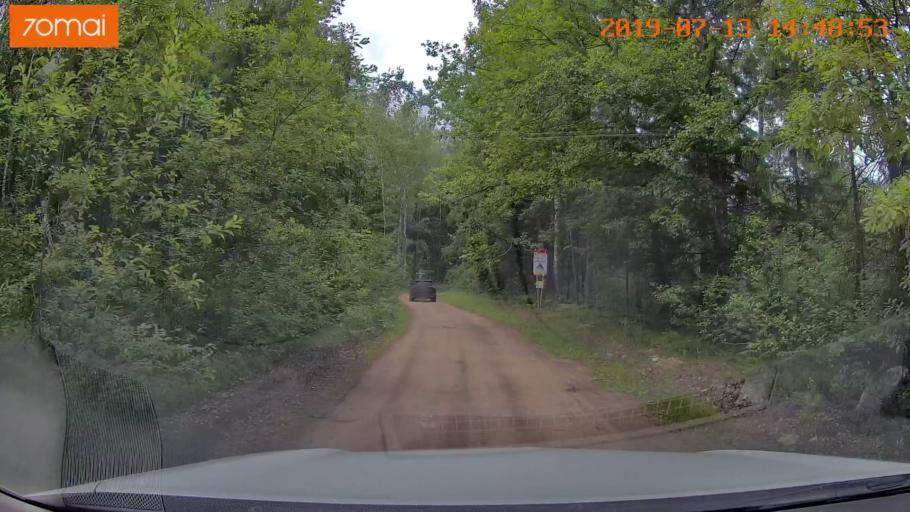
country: BY
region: Mogilev
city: Asipovichy
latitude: 53.2060
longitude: 28.7479
